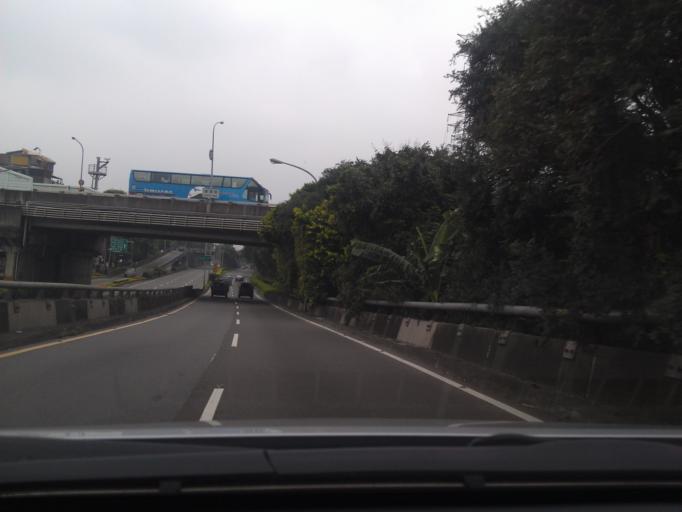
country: TW
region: Taipei
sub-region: Taipei
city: Banqiao
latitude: 25.0282
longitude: 121.4887
